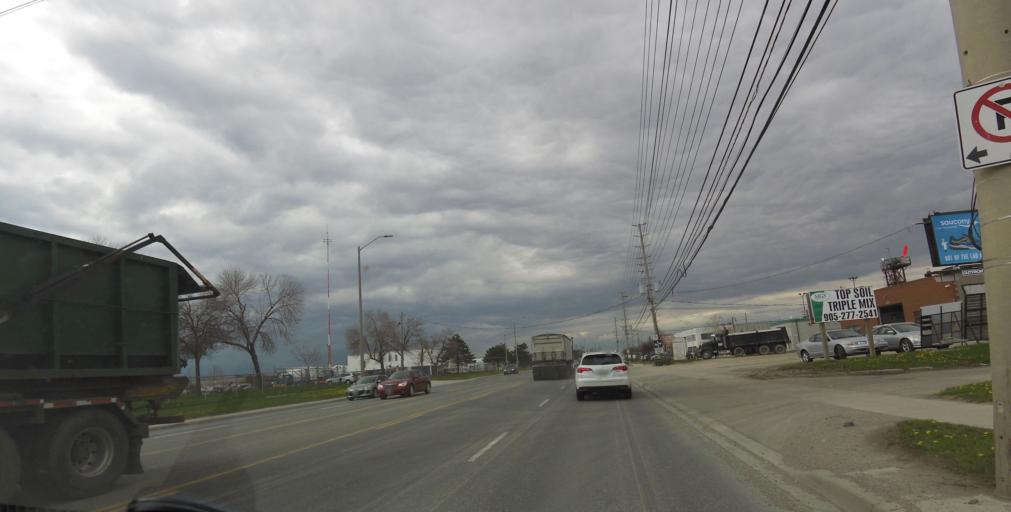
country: CA
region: Ontario
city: Mississauga
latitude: 43.5763
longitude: -79.6475
